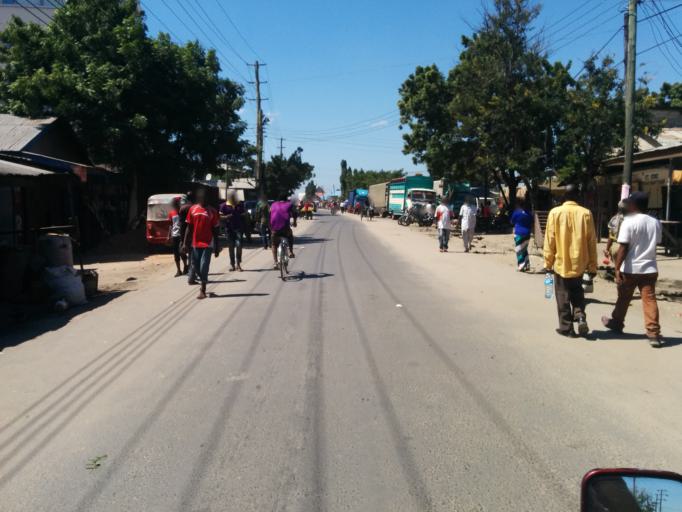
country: TZ
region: Dar es Salaam
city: Magomeni
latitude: -6.7964
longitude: 39.2367
